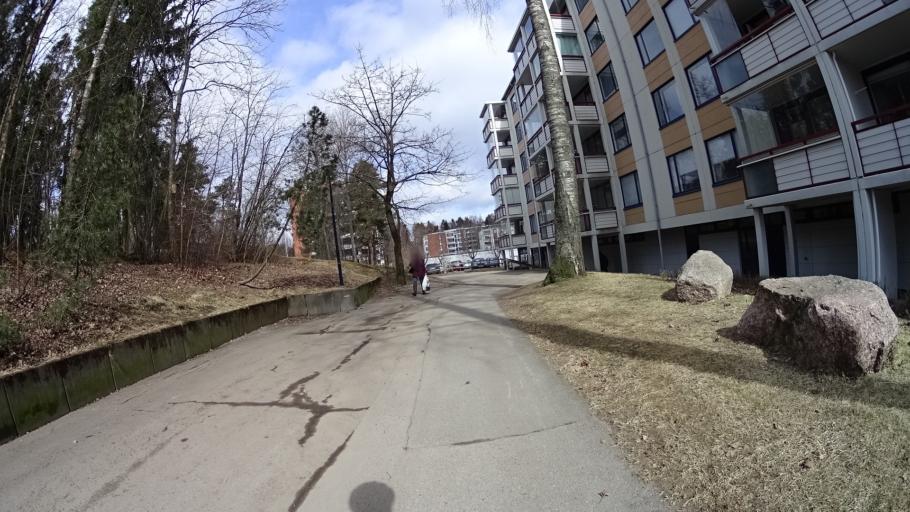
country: FI
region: Uusimaa
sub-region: Helsinki
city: Kilo
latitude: 60.2608
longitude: 24.8047
